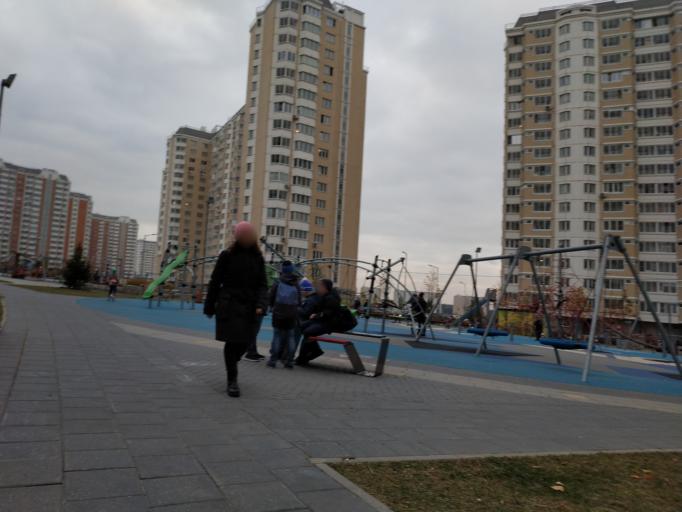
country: RU
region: Moscow
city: Novo-Peredelkino
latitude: 55.6370
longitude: 37.3254
